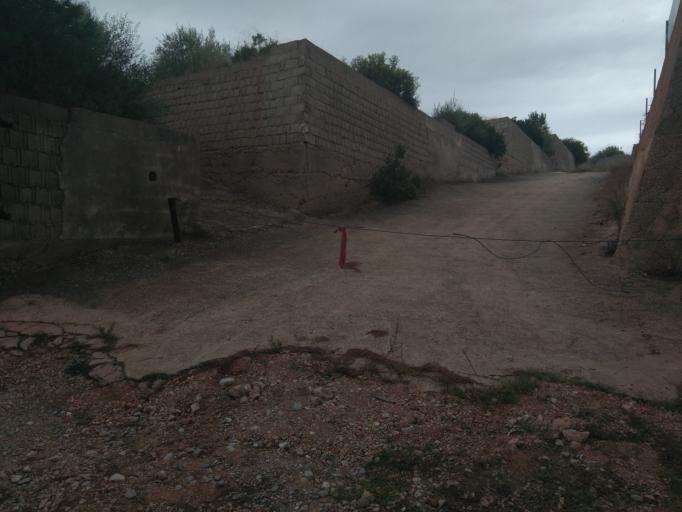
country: ES
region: Valencia
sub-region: Provincia de Valencia
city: Benimodo
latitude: 39.1939
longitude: -0.5691
